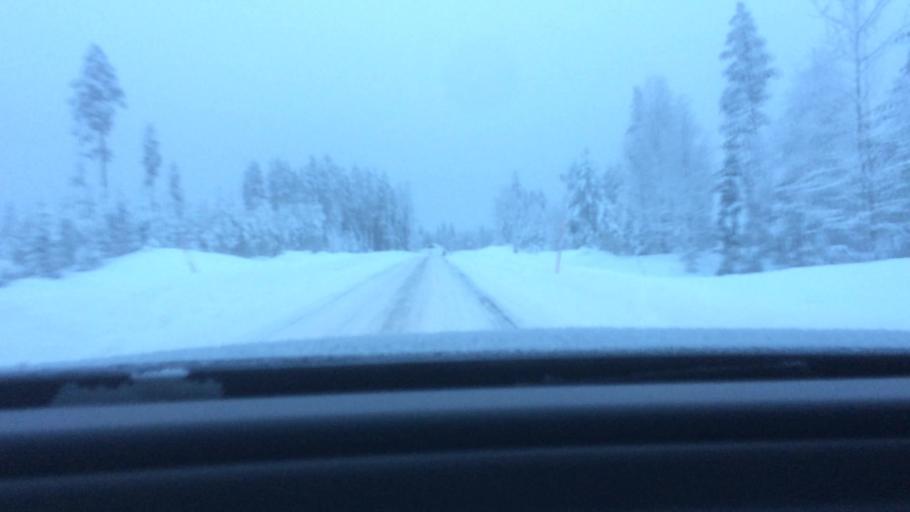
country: SE
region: Gaevleborg
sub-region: Ljusdals Kommun
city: Farila
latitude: 61.7752
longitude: 15.1726
